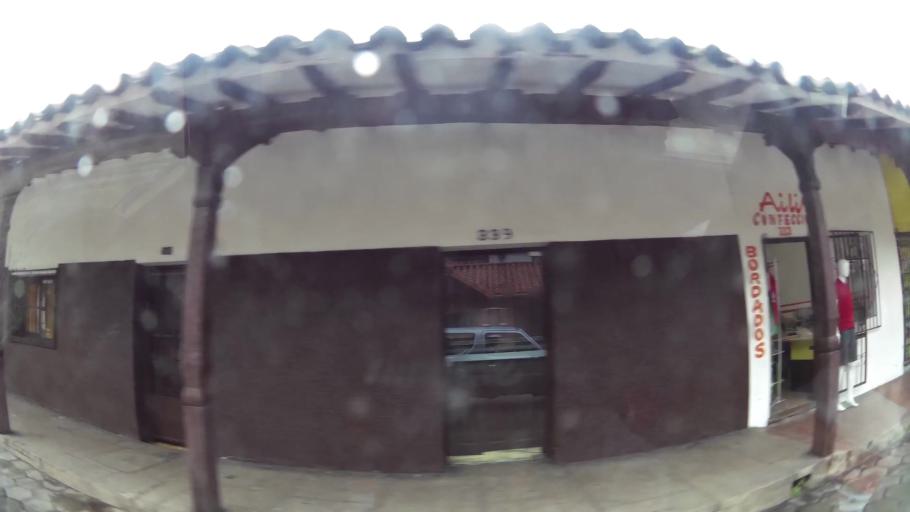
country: BO
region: Santa Cruz
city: Santa Cruz de la Sierra
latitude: -17.7886
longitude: -63.1846
